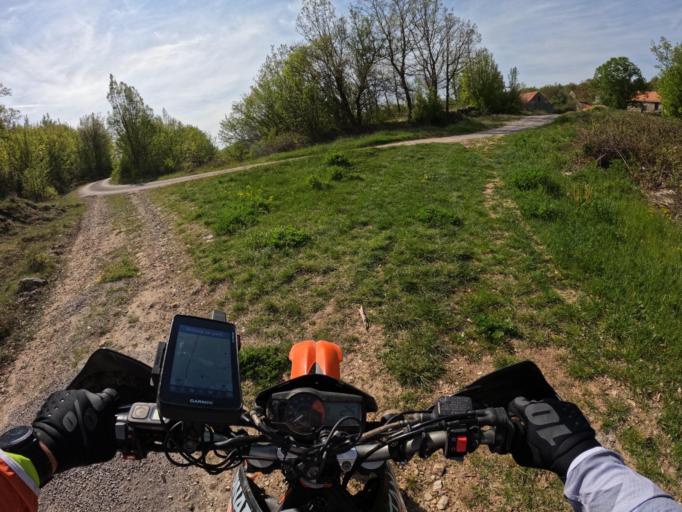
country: HR
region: Splitsko-Dalmatinska
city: Trilj
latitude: 43.5674
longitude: 16.7934
